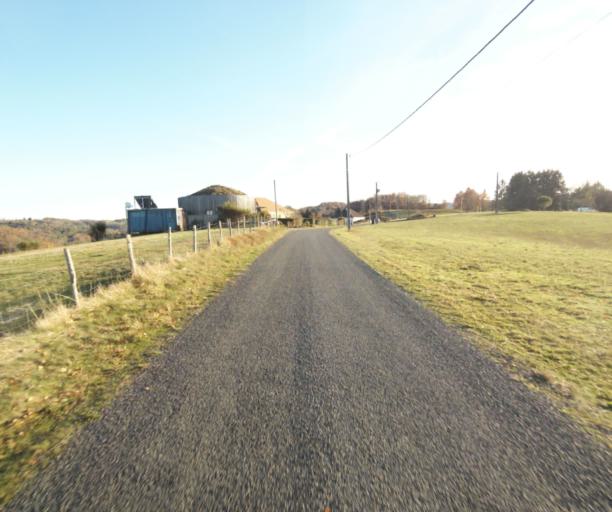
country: FR
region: Limousin
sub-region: Departement de la Correze
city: Laguenne
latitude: 45.2296
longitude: 1.8013
